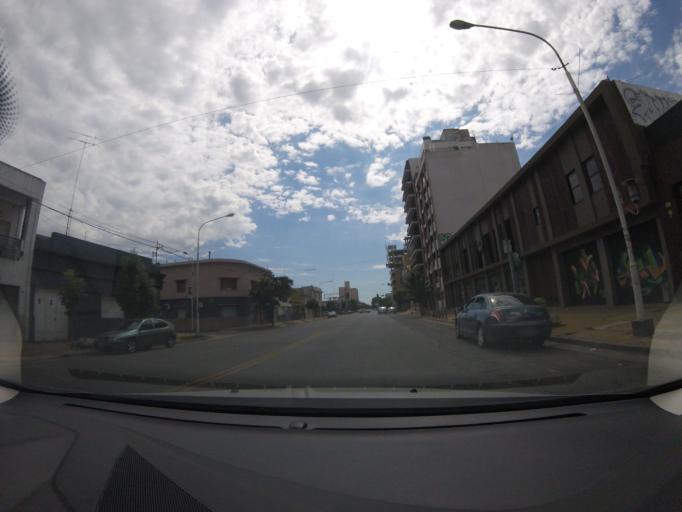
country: AR
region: Buenos Aires
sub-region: Partido de Tandil
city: Tandil
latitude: -37.3220
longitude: -59.1370
